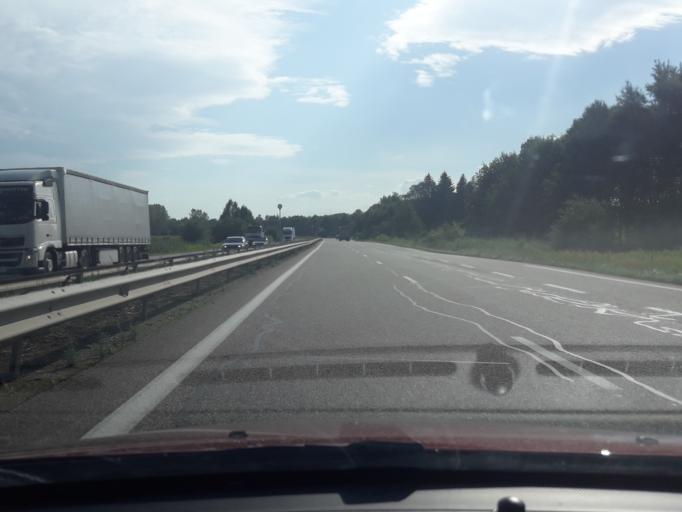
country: FR
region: Alsace
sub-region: Departement du Bas-Rhin
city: Kilstett
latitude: 48.6920
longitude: 7.8263
